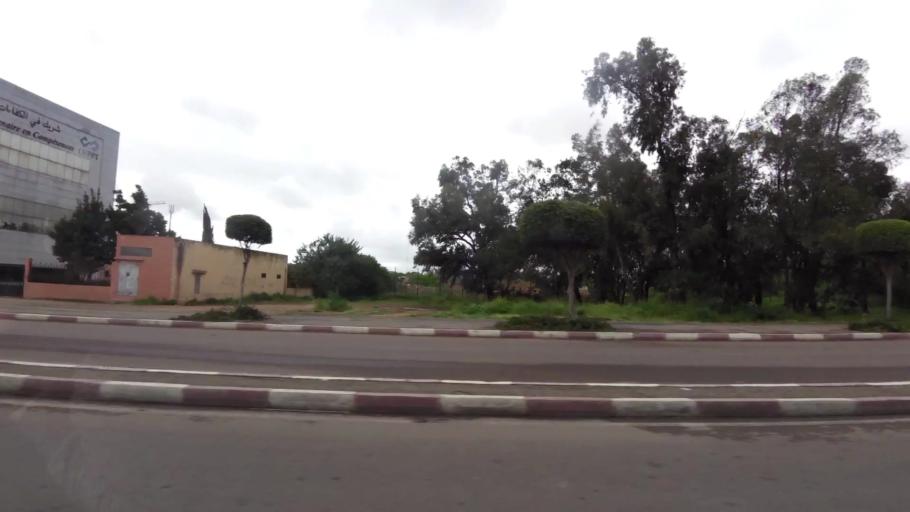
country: MA
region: Grand Casablanca
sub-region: Casablanca
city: Casablanca
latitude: 33.5234
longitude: -7.6350
